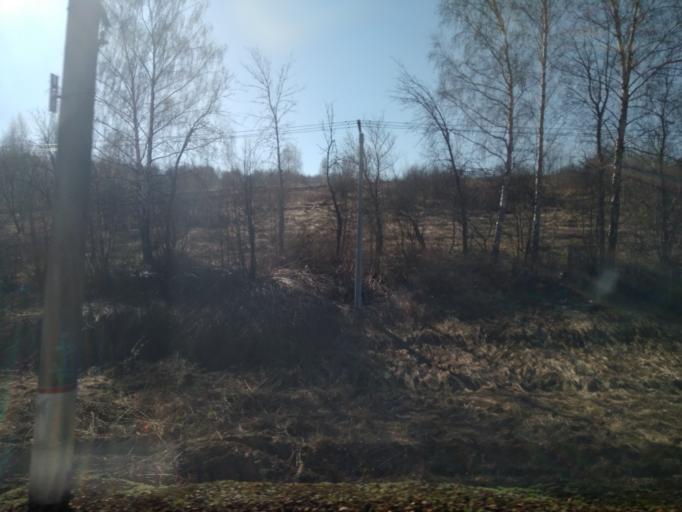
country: RU
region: Moskovskaya
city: Pavshino
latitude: 55.8240
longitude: 37.3615
